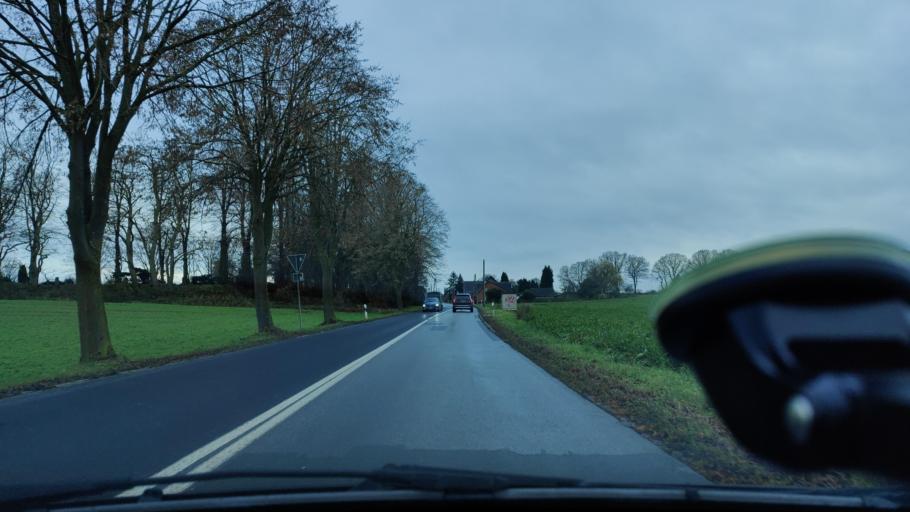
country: DE
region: North Rhine-Westphalia
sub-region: Regierungsbezirk Dusseldorf
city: Alpen
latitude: 51.5892
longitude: 6.4779
